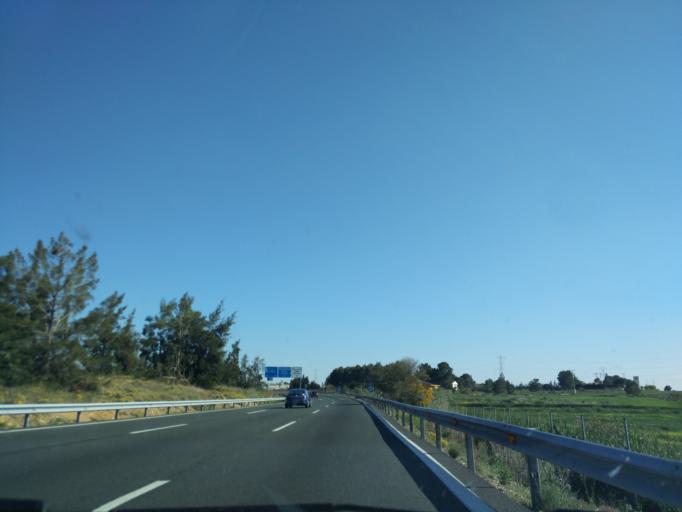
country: ES
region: Murcia
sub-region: Murcia
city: Murcia
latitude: 37.8891
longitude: -1.1410
